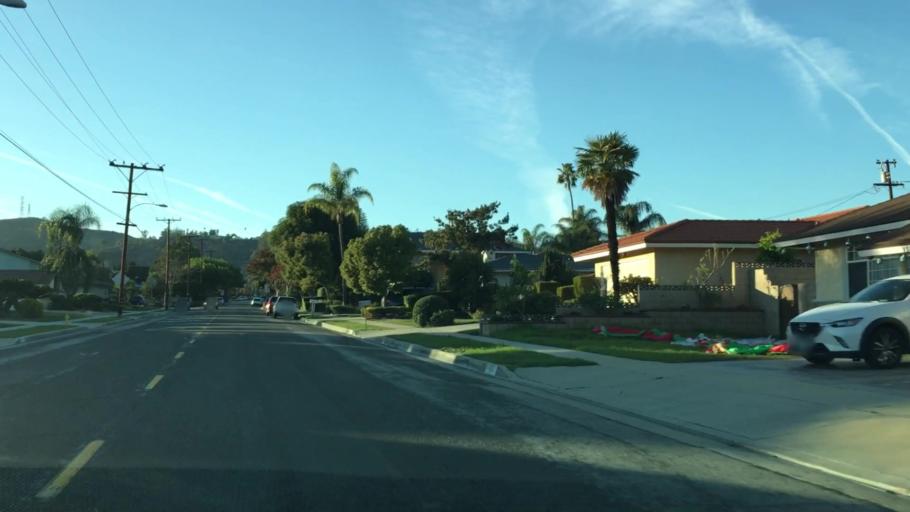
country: US
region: California
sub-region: Los Angeles County
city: Hacienda Heights
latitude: 33.9884
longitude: -117.9787
